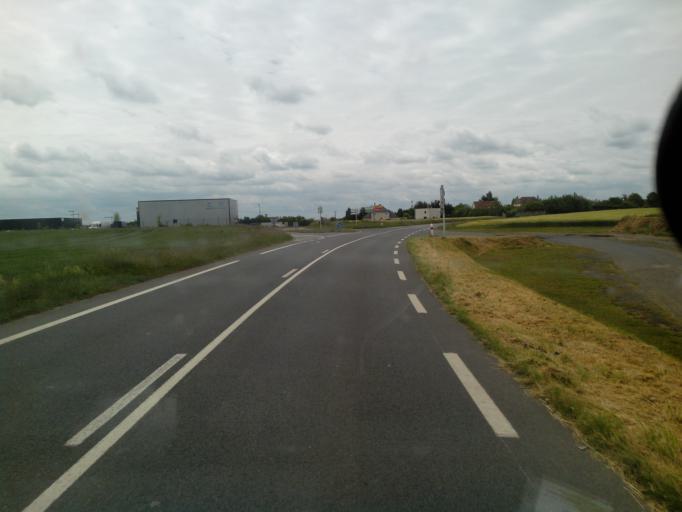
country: FR
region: Lower Normandy
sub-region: Departement du Calvados
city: Ranville
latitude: 49.2412
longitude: -0.2542
